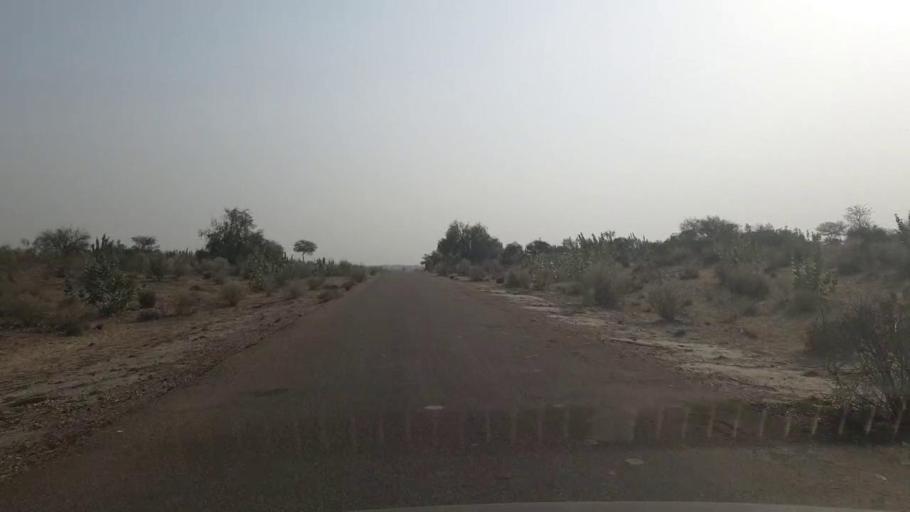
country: PK
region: Sindh
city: Chor
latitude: 25.4797
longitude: 69.9742
